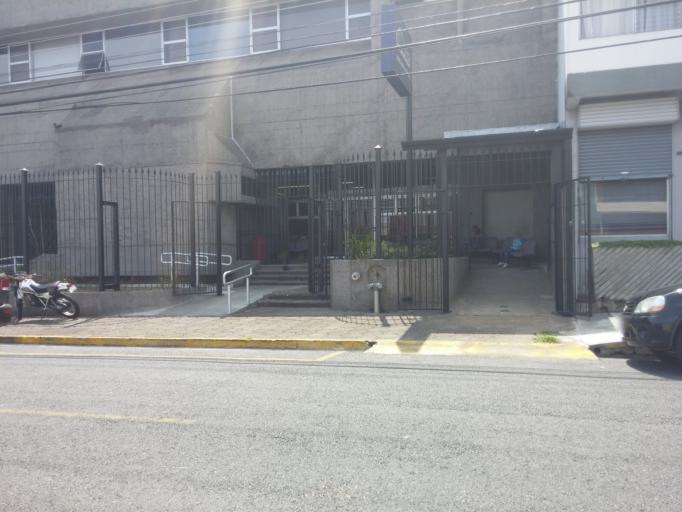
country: CR
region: Heredia
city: San Francisco
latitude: 9.9992
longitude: -84.1248
